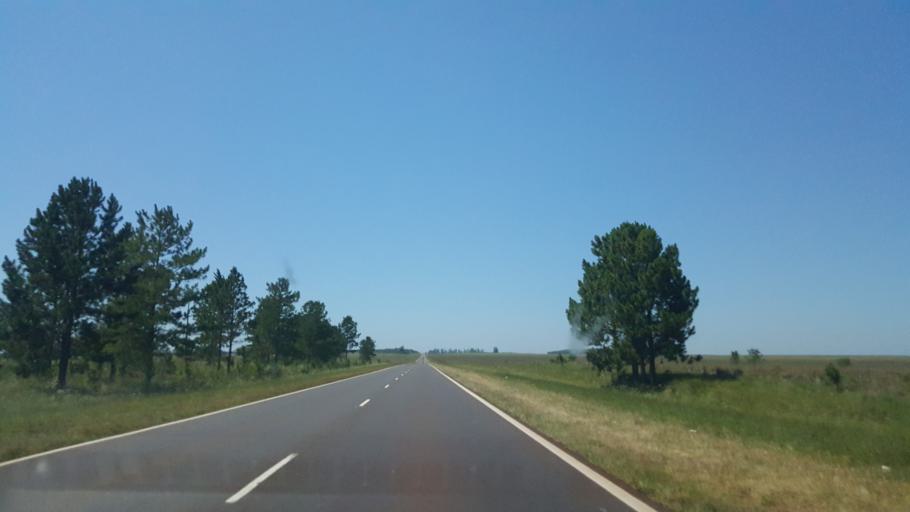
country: AR
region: Corrientes
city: Santo Tome
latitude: -28.3945
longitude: -56.1076
